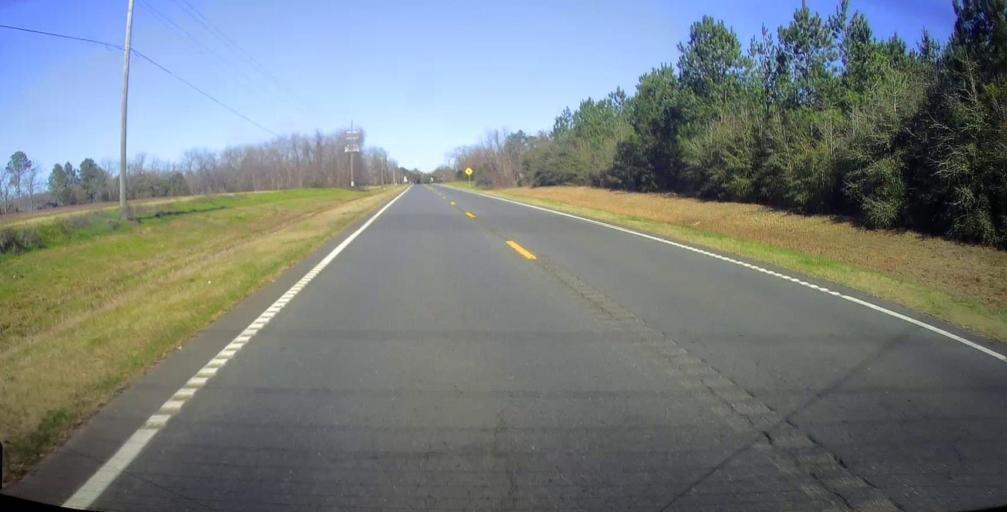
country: US
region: Georgia
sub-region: Macon County
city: Oglethorpe
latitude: 32.2993
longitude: -84.0732
